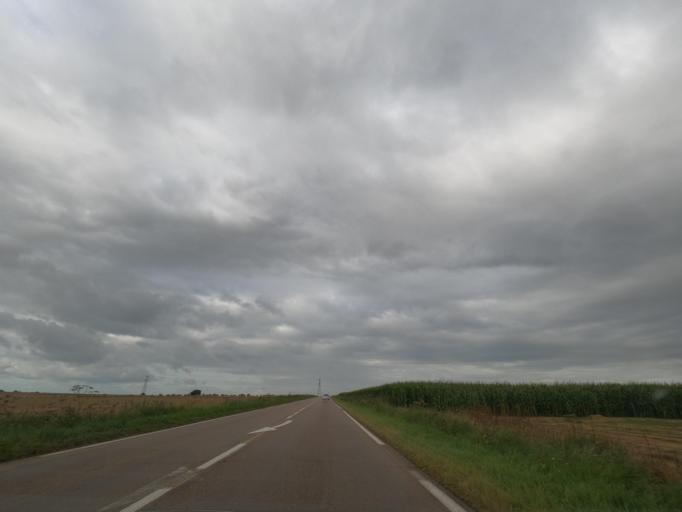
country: FR
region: Haute-Normandie
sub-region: Departement de l'Eure
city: Bourgtheroulde-Infreville
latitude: 49.2878
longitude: 0.8503
